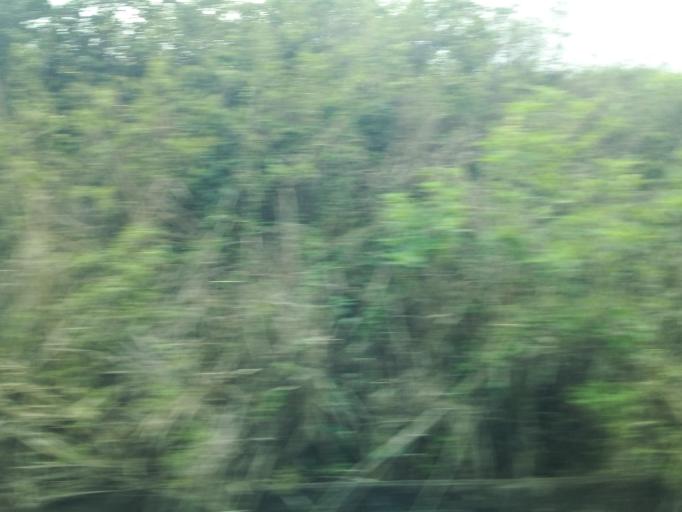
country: BR
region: Minas Gerais
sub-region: Ipatinga
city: Ipatinga
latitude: -19.4642
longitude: -42.4739
